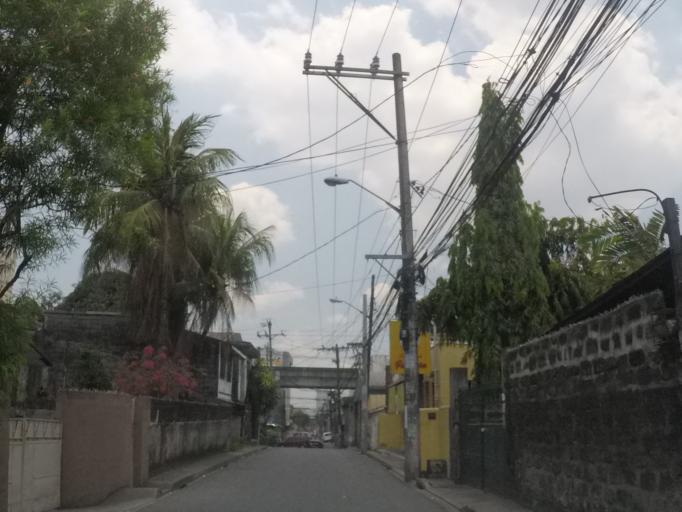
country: PH
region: Metro Manila
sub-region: San Juan
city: San Juan
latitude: 14.6097
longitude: 121.0259
